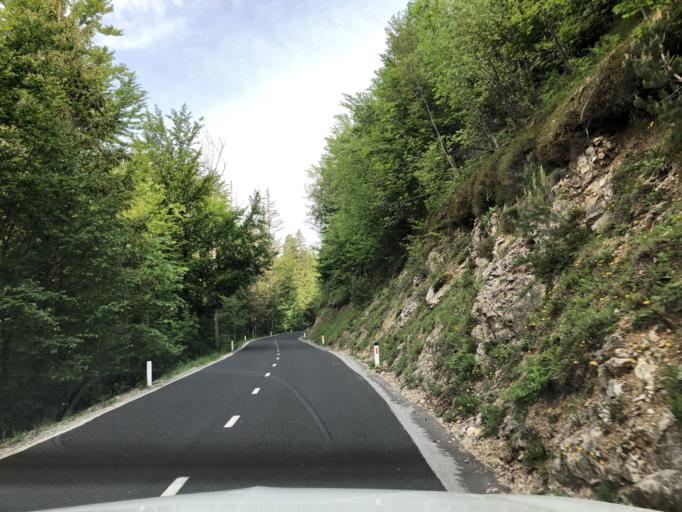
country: SI
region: Bloke
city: Nova Vas
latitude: 45.7988
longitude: 14.5577
